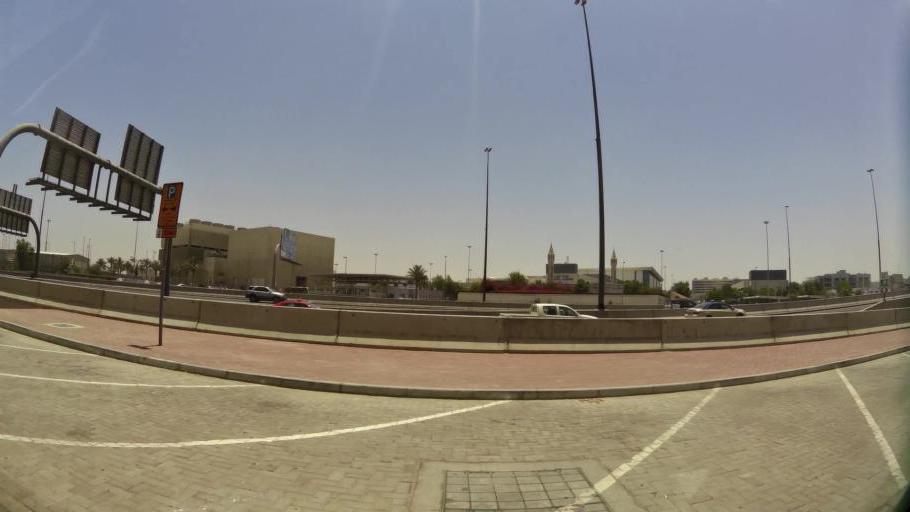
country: AE
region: Ash Shariqah
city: Sharjah
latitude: 25.2582
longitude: 55.3370
